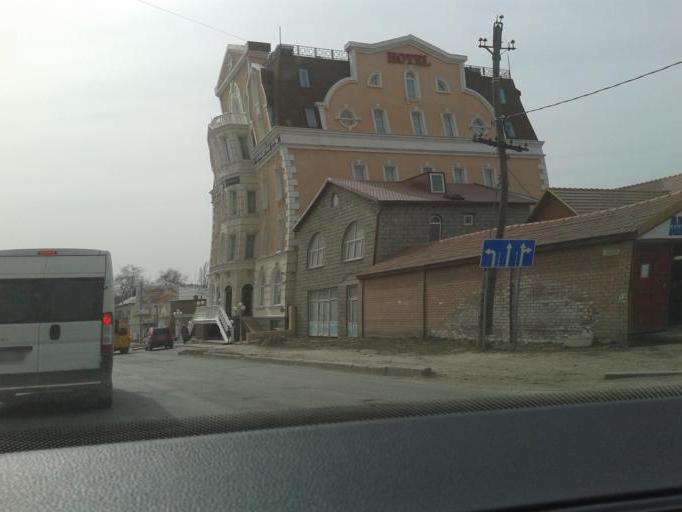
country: RU
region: Volgograd
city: Volgograd
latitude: 48.7151
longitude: 44.4996
